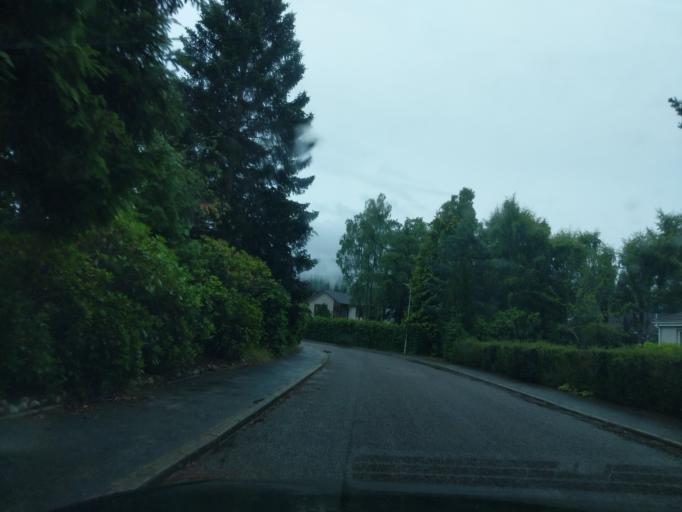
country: GB
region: Scotland
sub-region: Aberdeenshire
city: Aboyne
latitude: 57.0728
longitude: -2.7998
